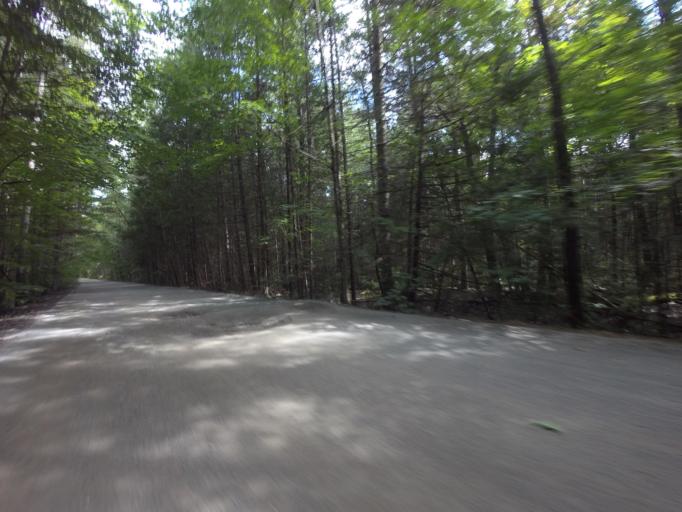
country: CA
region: Ontario
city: Omemee
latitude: 44.6939
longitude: -78.6912
